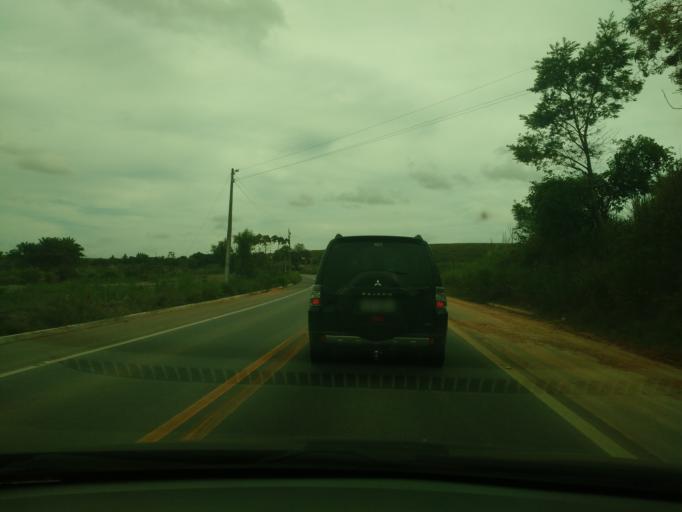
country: BR
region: Alagoas
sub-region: Messias
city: Messias
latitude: -9.3651
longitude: -35.8496
